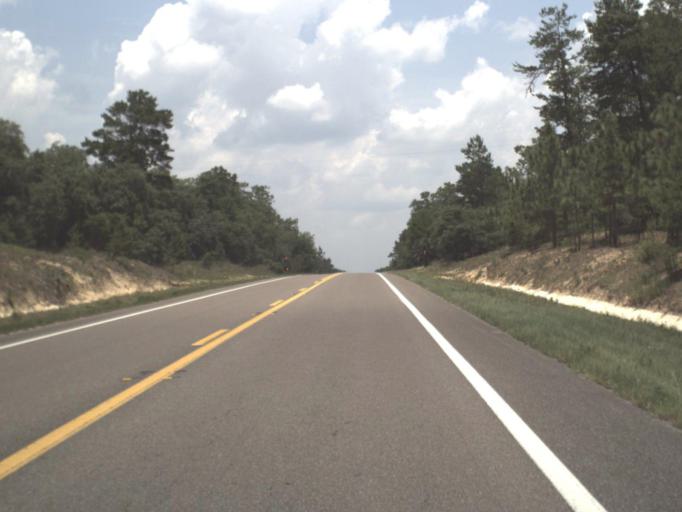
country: US
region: Florida
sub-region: Putnam County
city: Crescent City
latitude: 29.4272
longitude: -81.7374
